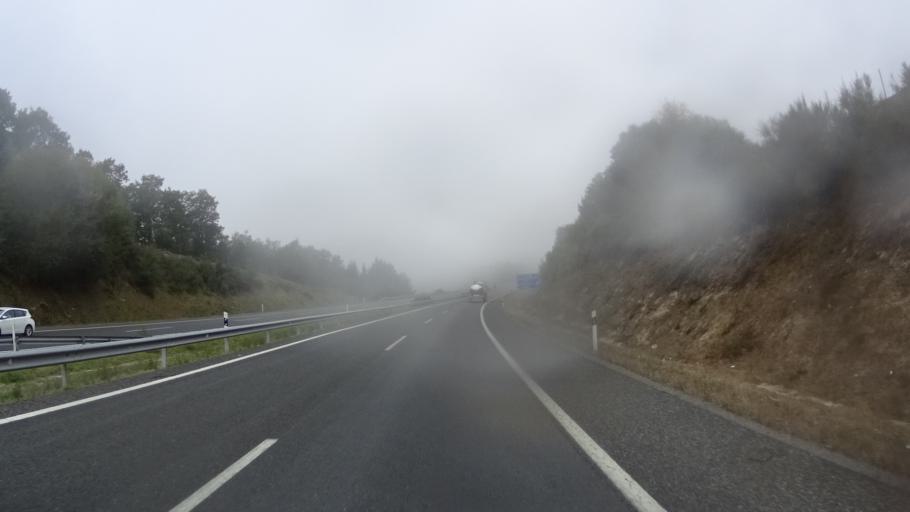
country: ES
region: Galicia
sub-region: Provincia de Lugo
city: Corgo
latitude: 42.9316
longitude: -7.3785
